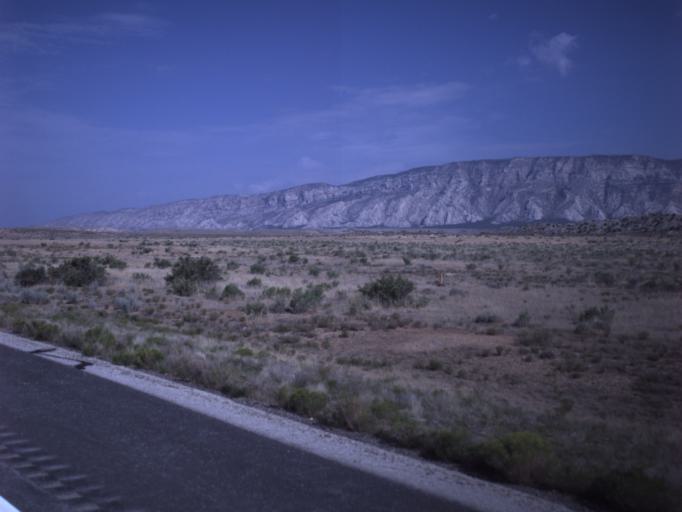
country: US
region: Colorado
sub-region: Rio Blanco County
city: Rangely
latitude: 40.2827
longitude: -109.0955
